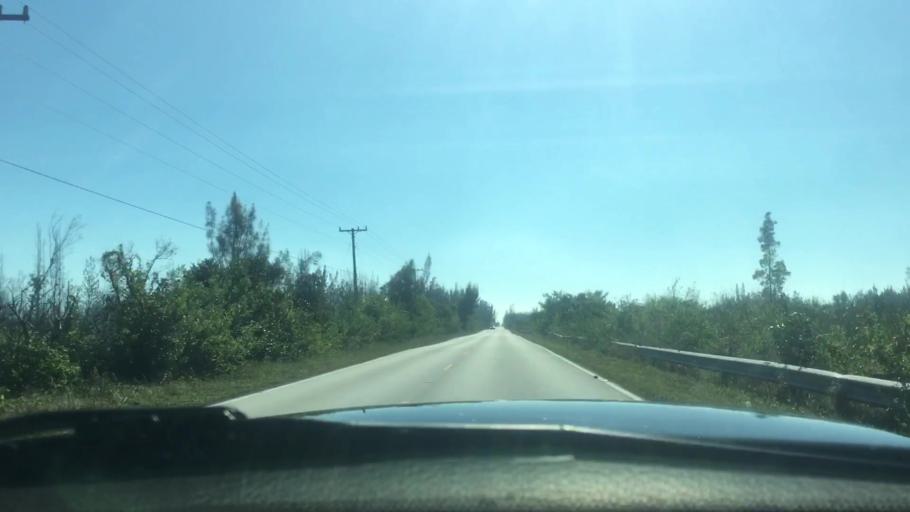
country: US
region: Florida
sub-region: Miami-Dade County
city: Florida City
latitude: 25.4243
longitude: -80.4672
